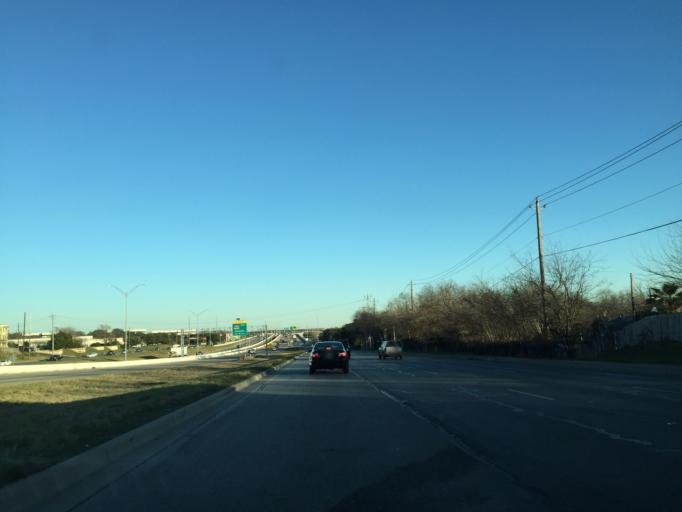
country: US
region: Texas
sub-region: Travis County
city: Austin
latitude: 30.3354
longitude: -97.6934
